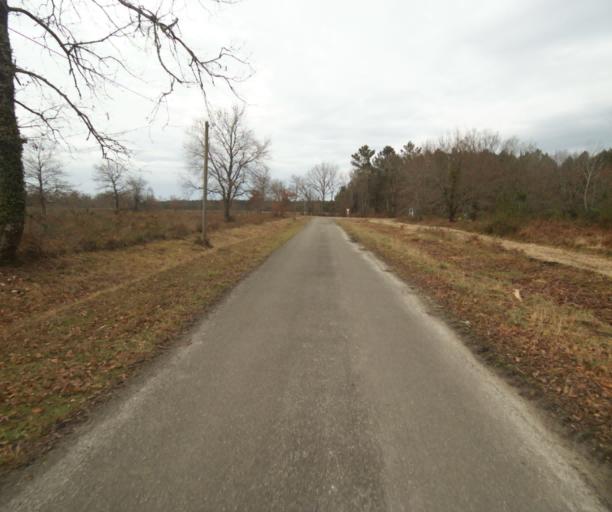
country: FR
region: Aquitaine
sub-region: Departement des Landes
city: Gabarret
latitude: 44.0379
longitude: -0.0742
